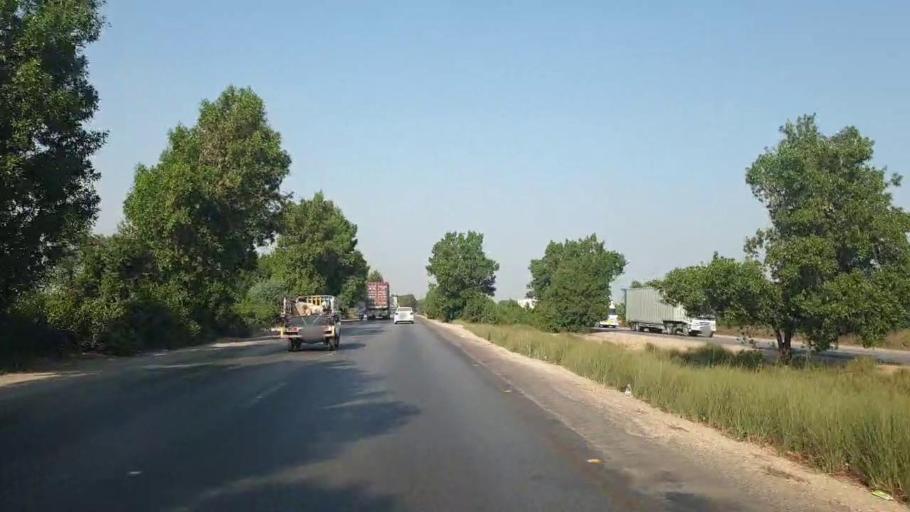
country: PK
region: Sindh
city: Matiari
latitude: 25.5061
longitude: 68.4267
